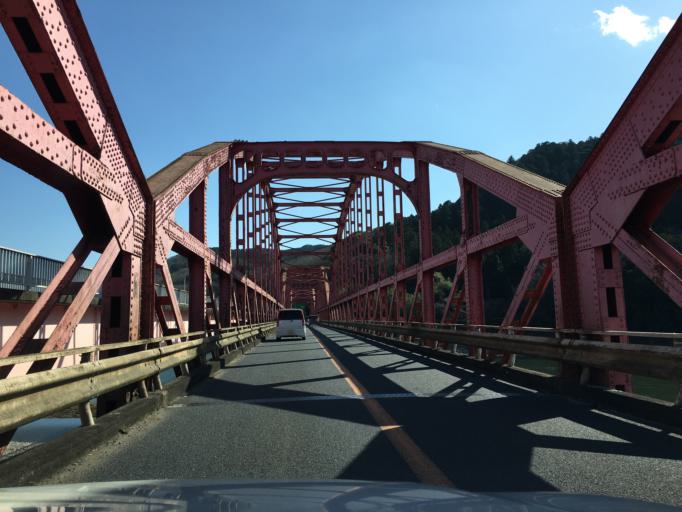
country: JP
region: Ibaraki
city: Omiya
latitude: 36.5471
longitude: 140.3321
